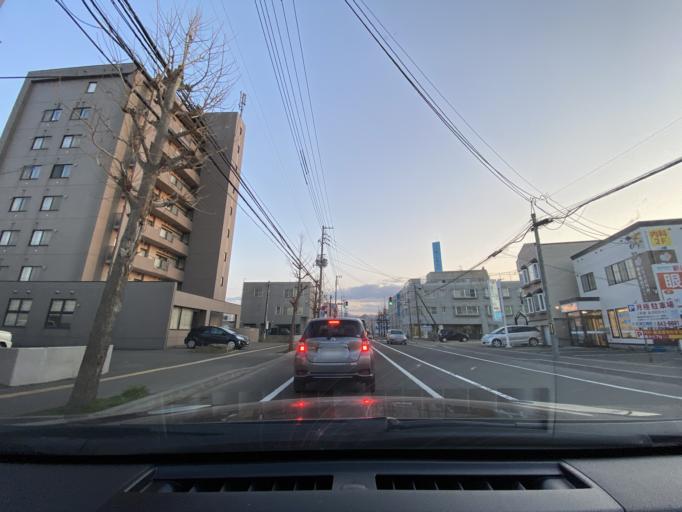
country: JP
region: Hokkaido
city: Sapporo
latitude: 43.0942
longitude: 141.3216
